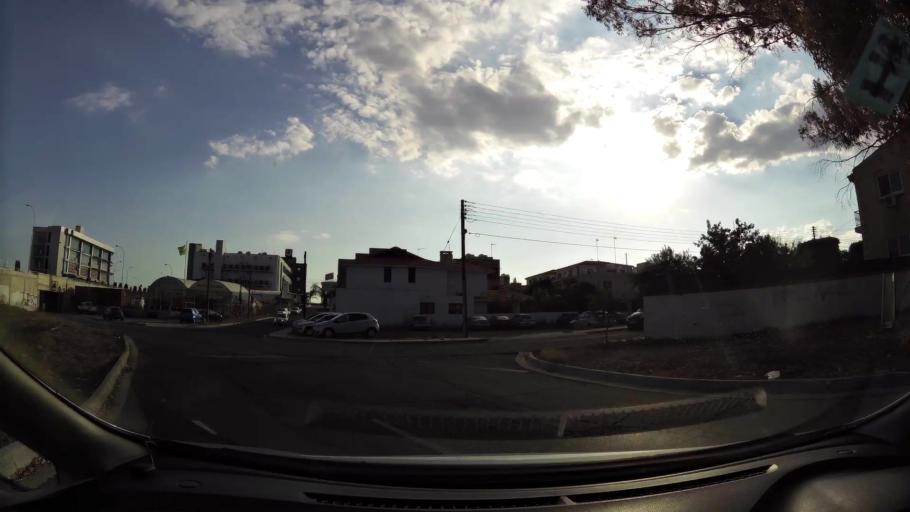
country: CY
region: Larnaka
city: Larnaca
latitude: 34.9302
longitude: 33.6043
